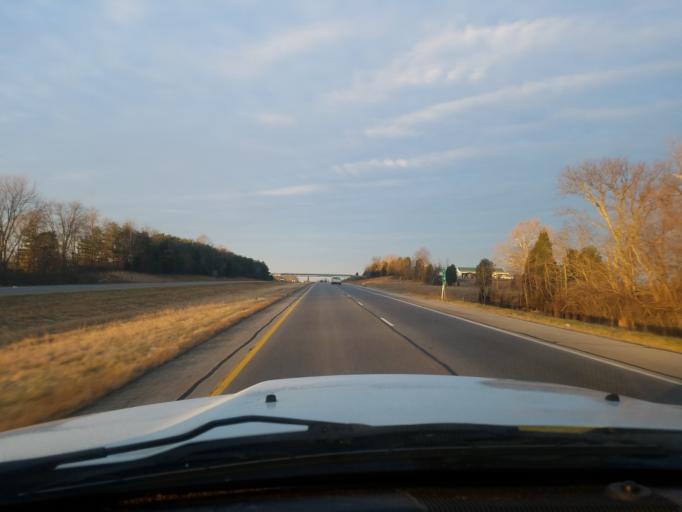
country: US
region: Indiana
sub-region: Floyd County
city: Georgetown
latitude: 38.2710
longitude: -85.9782
